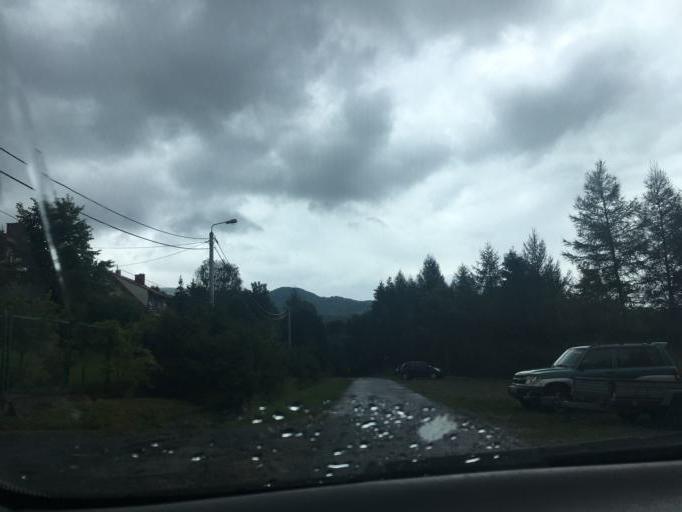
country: PL
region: Subcarpathian Voivodeship
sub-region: Powiat bieszczadzki
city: Lutowiska
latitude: 49.1035
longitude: 22.6546
